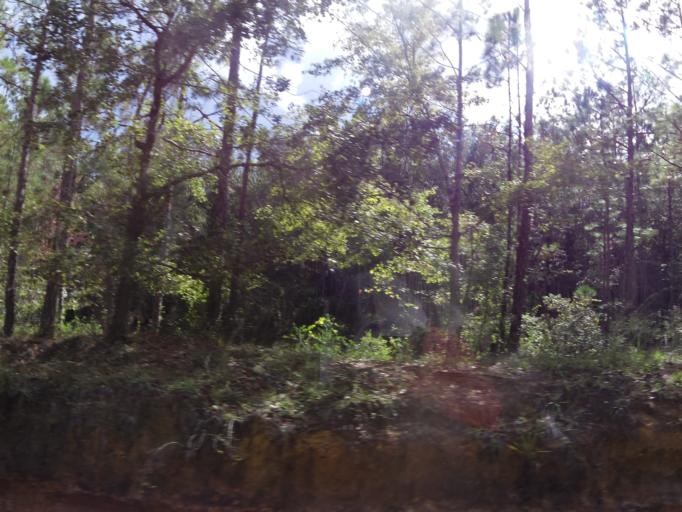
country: US
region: Florida
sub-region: Nassau County
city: Hilliard
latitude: 30.6066
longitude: -82.0739
